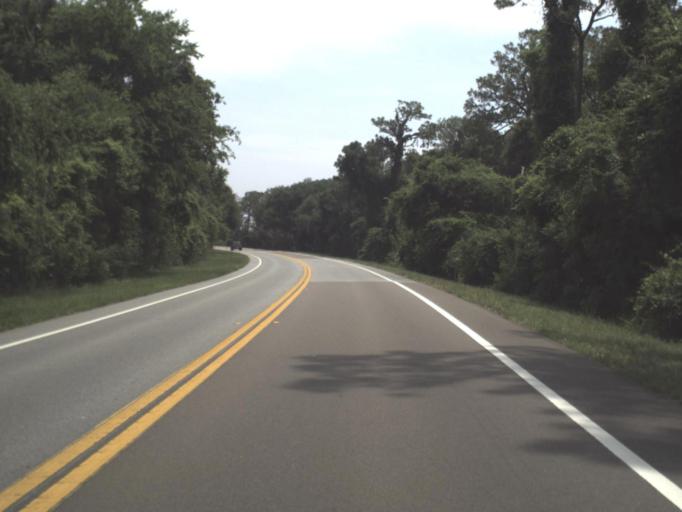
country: US
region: Florida
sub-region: Duval County
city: Atlantic Beach
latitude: 30.4653
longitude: -81.4368
